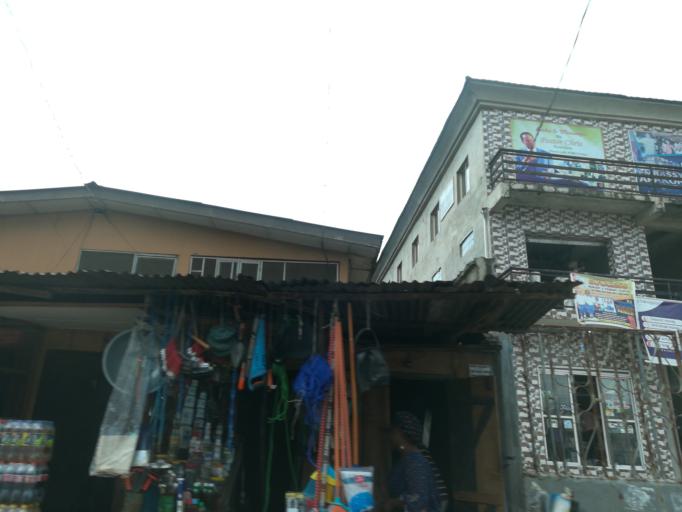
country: NG
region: Lagos
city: Oshodi
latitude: 6.5507
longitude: 3.3356
